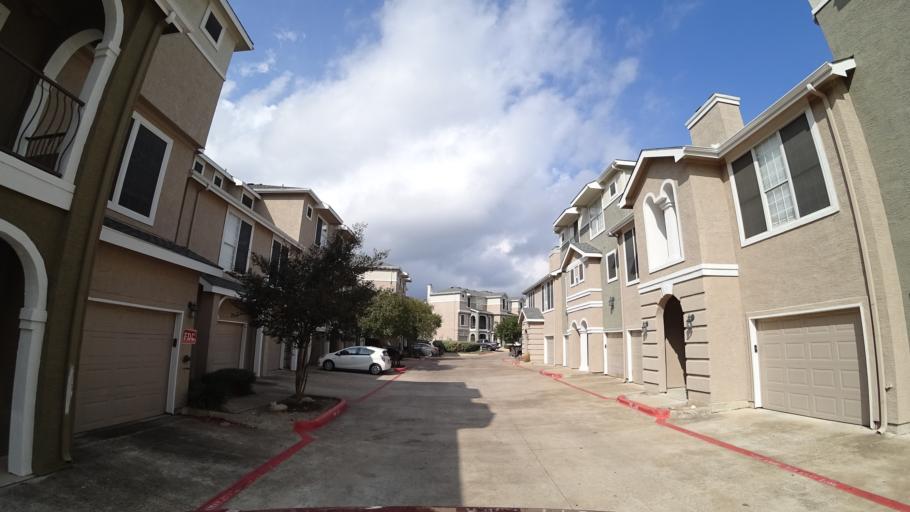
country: US
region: Texas
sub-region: Travis County
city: Hudson Bend
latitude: 30.3831
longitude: -97.8807
